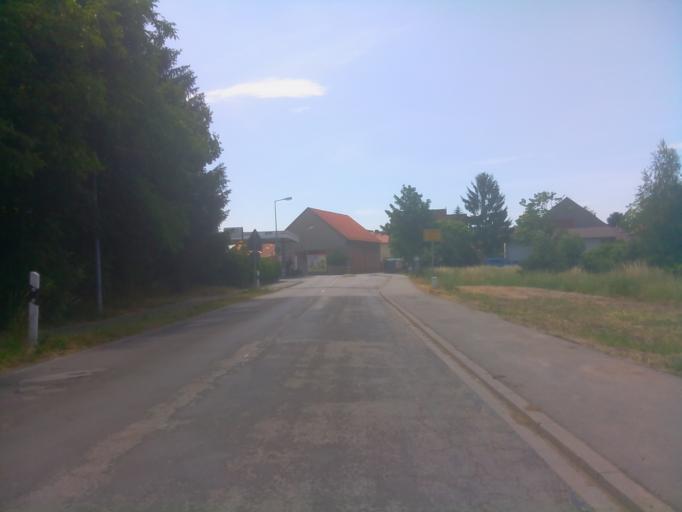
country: DE
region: Hesse
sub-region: Regierungsbezirk Darmstadt
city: Einhausen
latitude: 49.7004
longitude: 8.5694
